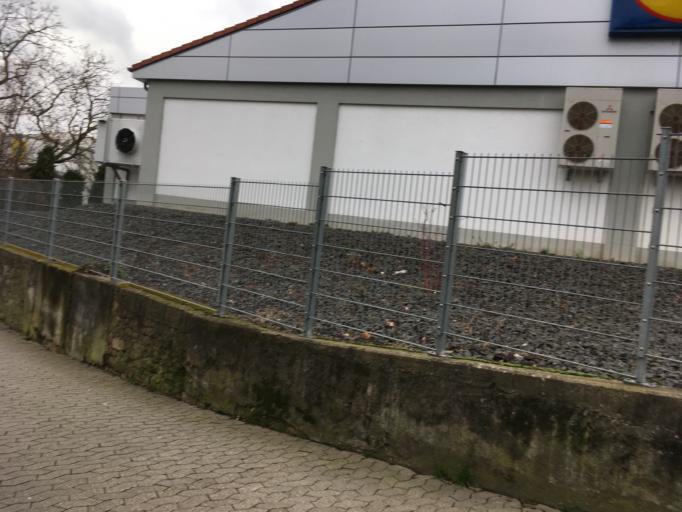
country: DE
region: Rheinland-Pfalz
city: Bad Kreuznach
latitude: 49.8501
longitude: 7.8644
